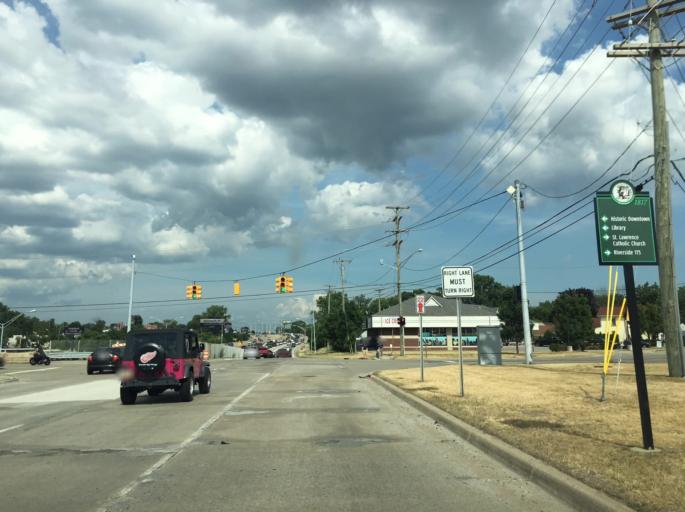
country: US
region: Michigan
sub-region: Macomb County
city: Utica
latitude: 42.6246
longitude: -83.0418
